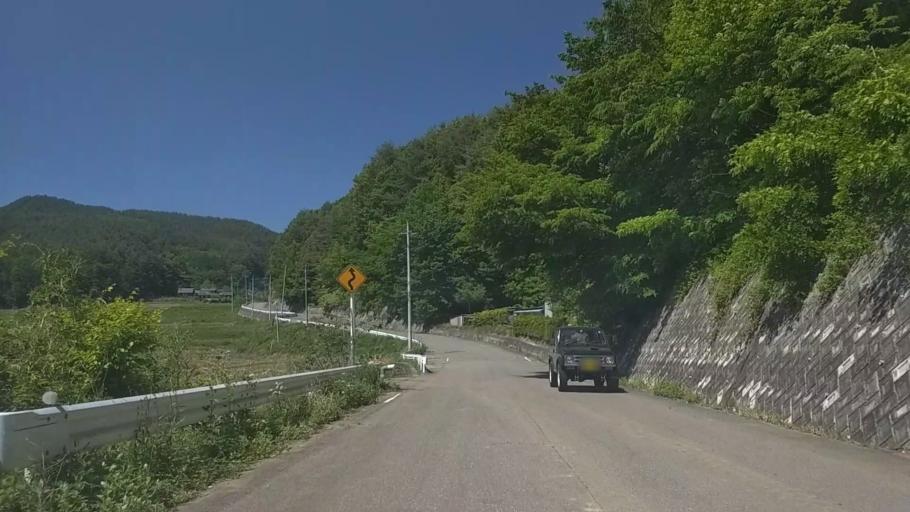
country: JP
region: Yamanashi
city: Nirasaki
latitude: 35.8566
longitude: 138.4471
